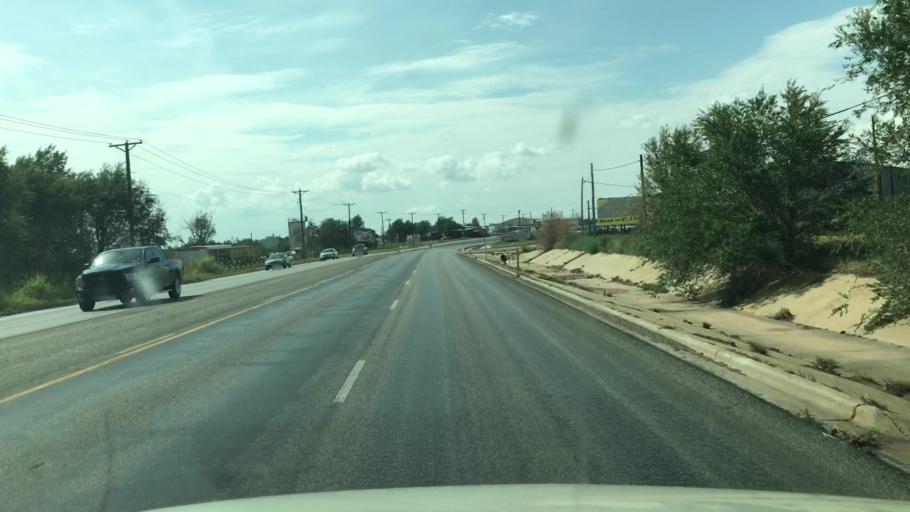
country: US
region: Texas
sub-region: Dawson County
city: Lamesa
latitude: 32.7183
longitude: -101.9429
